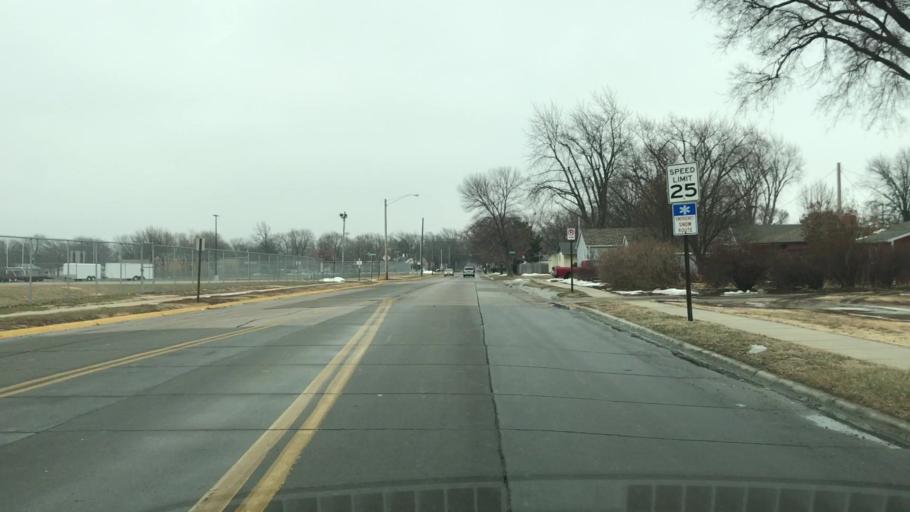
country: US
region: Nebraska
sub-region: Hall County
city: Grand Island
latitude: 40.9385
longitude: -98.3680
